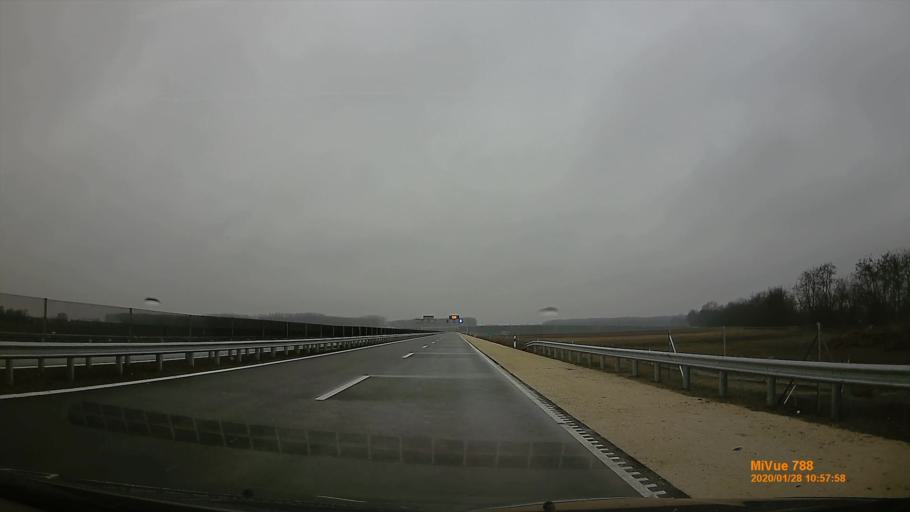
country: HU
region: Pest
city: Peteri
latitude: 47.3746
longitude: 19.4070
